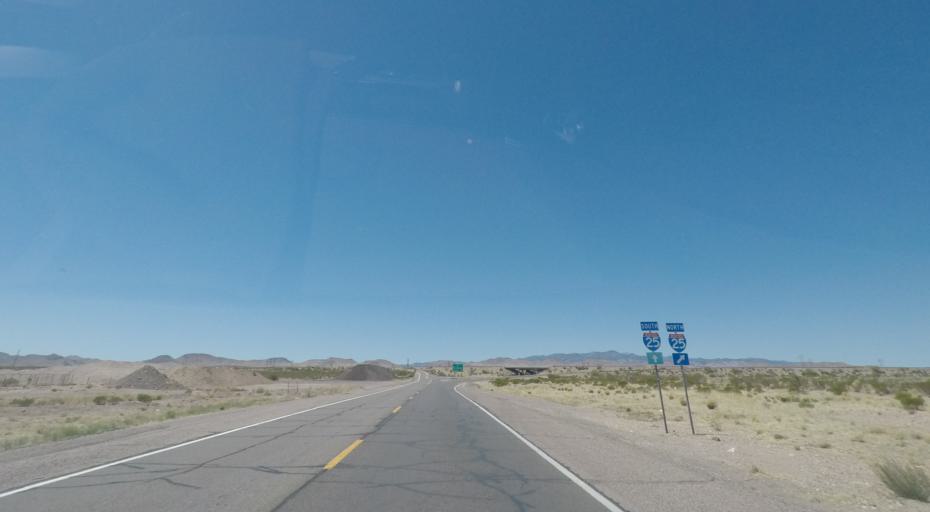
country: US
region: New Mexico
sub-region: Socorro County
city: Socorro
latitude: 33.9173
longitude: -106.8744
